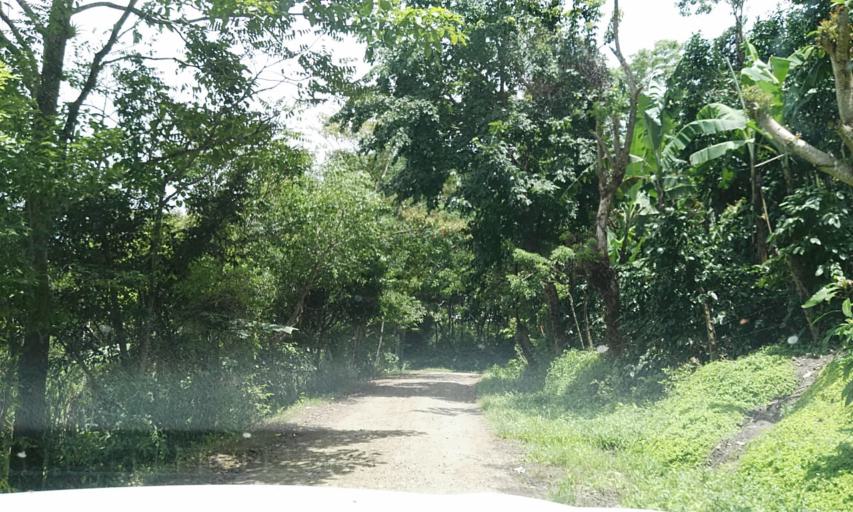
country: NI
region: Matagalpa
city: San Ramon
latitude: 12.9925
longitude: -85.8624
